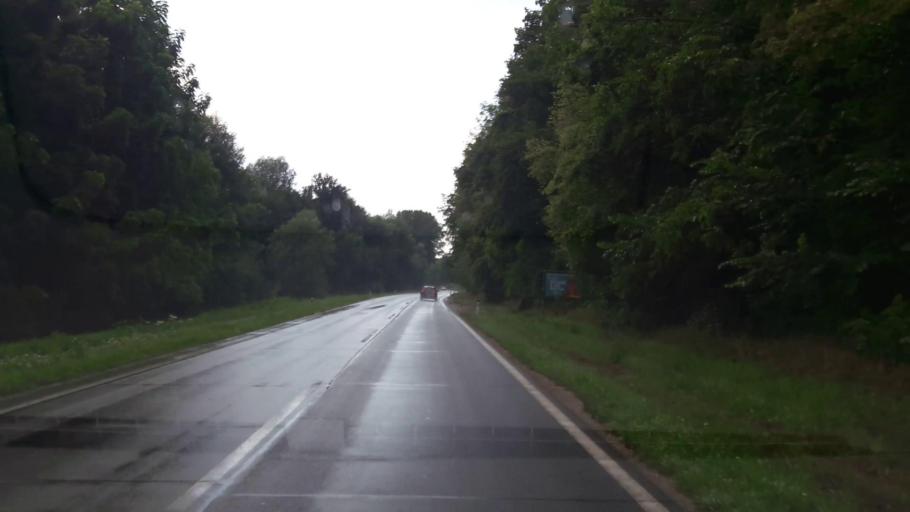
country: AT
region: Lower Austria
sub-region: Politischer Bezirk Melk
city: Emmersdorf an der Donau
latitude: 48.2493
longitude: 15.3483
